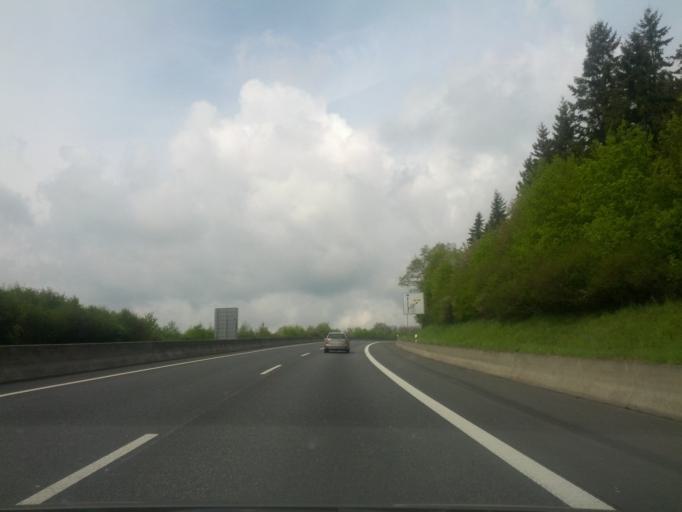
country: DE
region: Thuringia
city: Dankmarshausen
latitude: 50.9577
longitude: 10.0292
